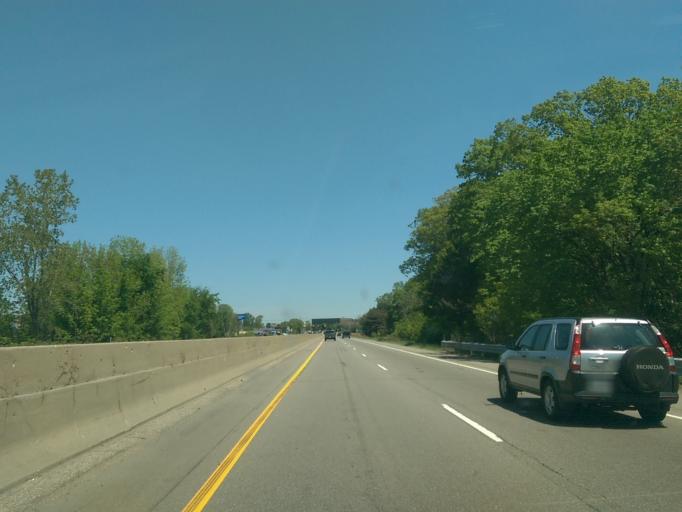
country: US
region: Michigan
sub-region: Ottawa County
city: Holland
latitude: 42.7656
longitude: -86.0901
